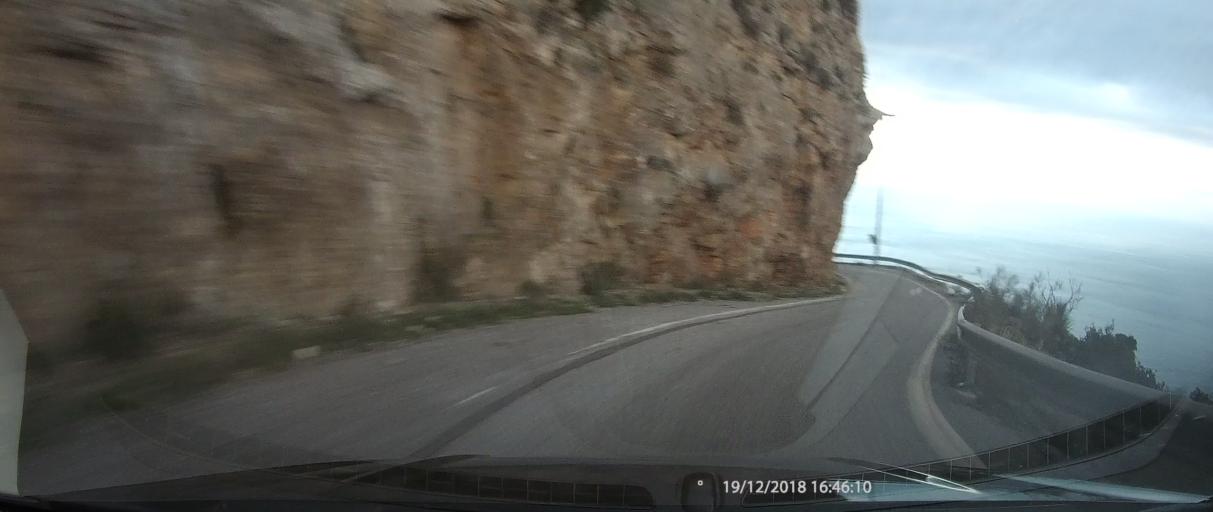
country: GR
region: Peloponnese
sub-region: Nomos Lakonias
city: Sykea
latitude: 36.9219
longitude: 23.0080
